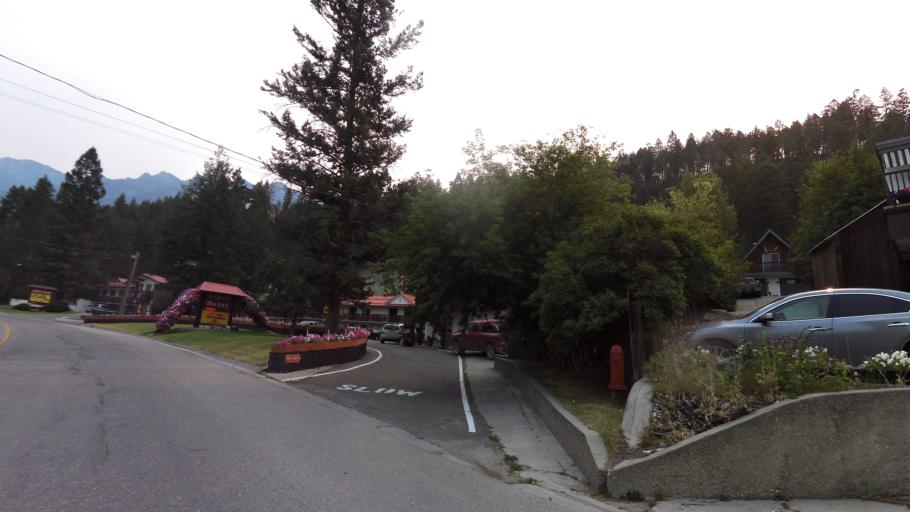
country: CA
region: British Columbia
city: Invermere
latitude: 50.6262
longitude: -116.0665
